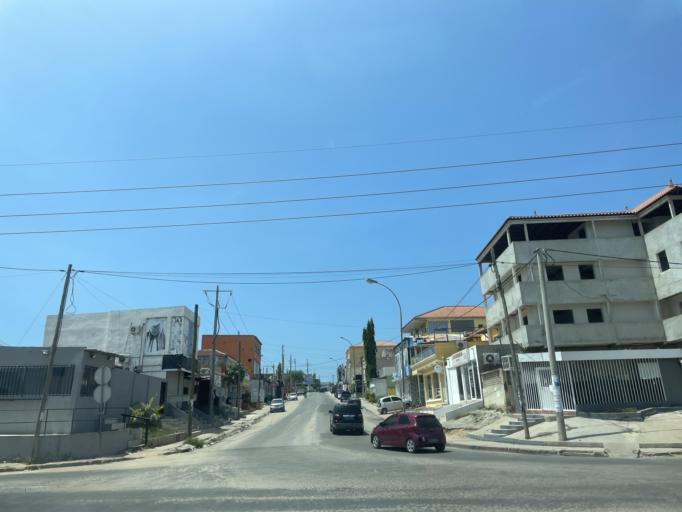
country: AO
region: Luanda
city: Luanda
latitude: -8.9156
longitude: 13.2029
